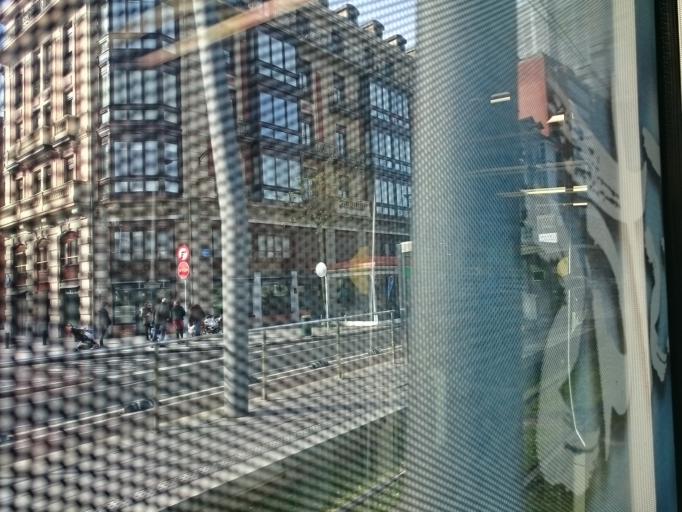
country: ES
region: Basque Country
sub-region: Bizkaia
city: Bilbao
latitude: 43.2643
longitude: -2.9260
